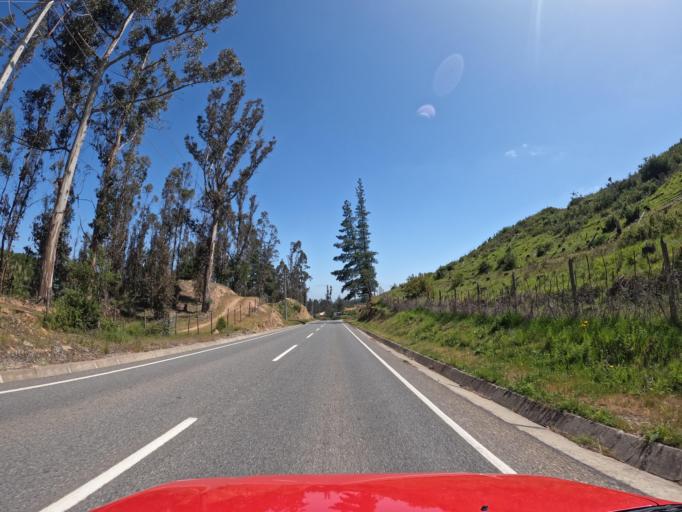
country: CL
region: O'Higgins
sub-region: Provincia de Colchagua
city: Santa Cruz
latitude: -34.6785
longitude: -71.7952
